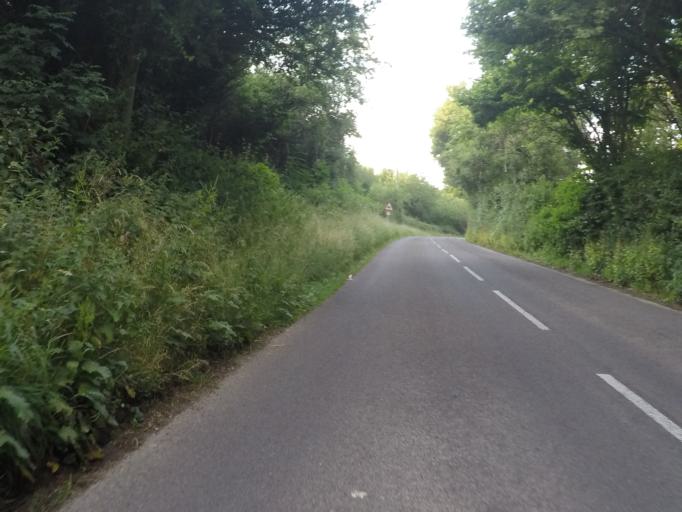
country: GB
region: England
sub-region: Oxfordshire
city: Charlbury
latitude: 51.8784
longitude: -1.4869
